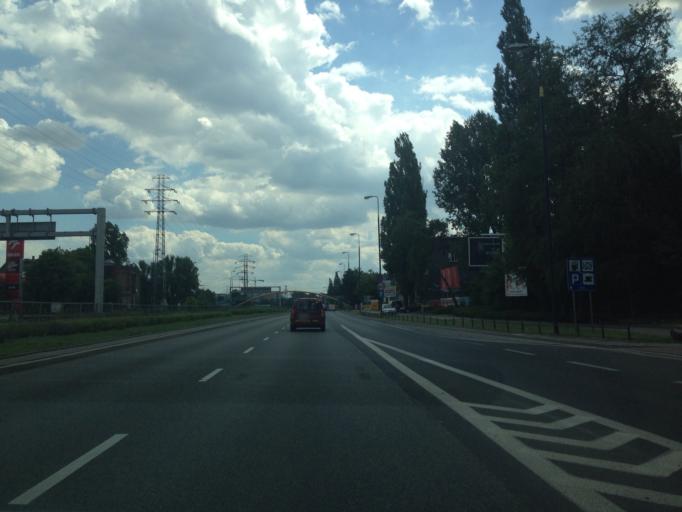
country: PL
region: Masovian Voivodeship
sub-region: Warszawa
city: Ochota
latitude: 52.2262
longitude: 20.9574
